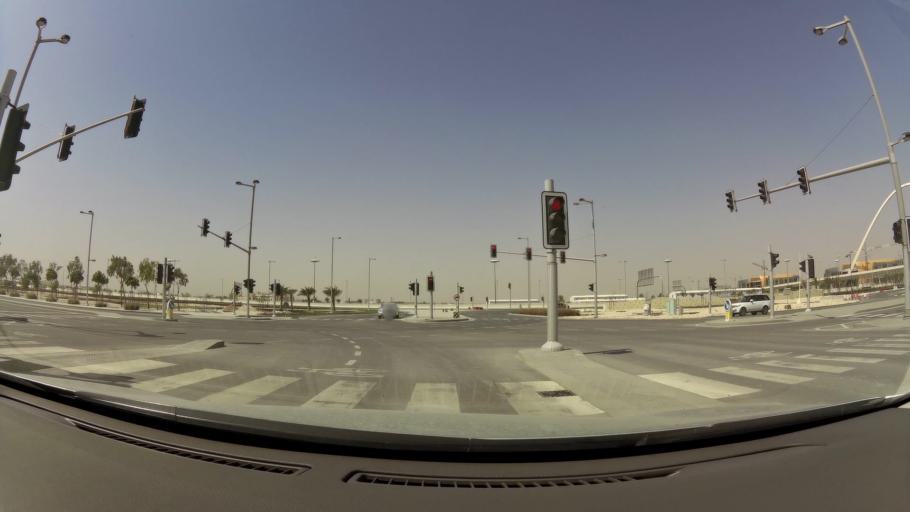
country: QA
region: Baladiyat Umm Salal
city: Umm Salal Muhammad
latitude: 25.3981
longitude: 51.5172
